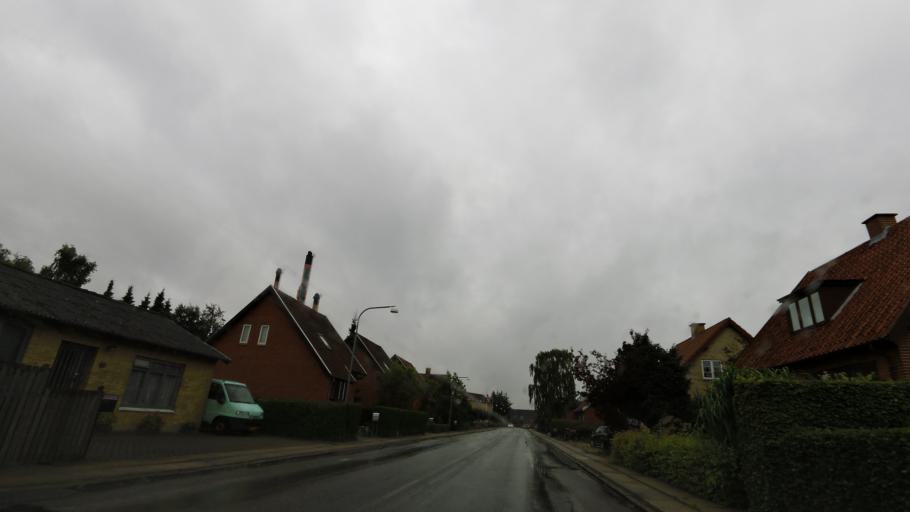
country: DK
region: South Denmark
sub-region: Nordfyns Kommune
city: Otterup
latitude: 55.5147
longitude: 10.4017
